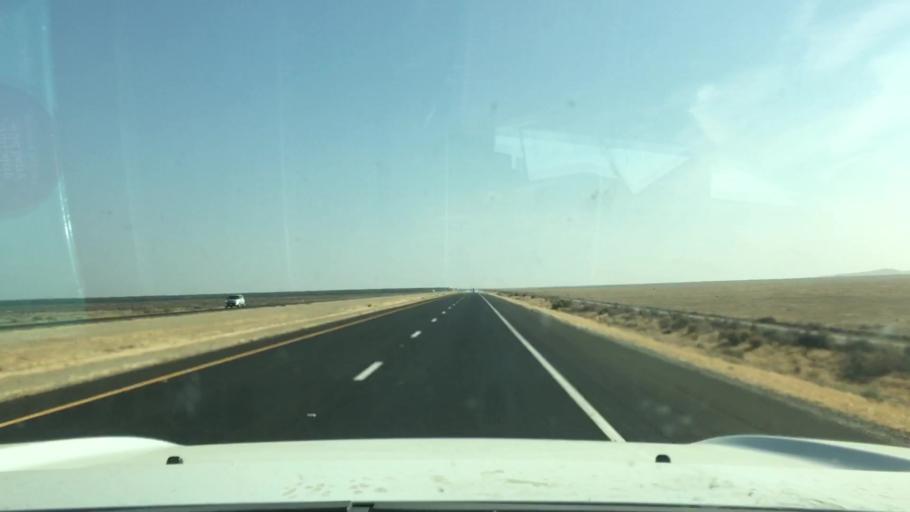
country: US
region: California
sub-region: Kern County
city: Lost Hills
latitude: 35.6249
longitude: -119.9866
